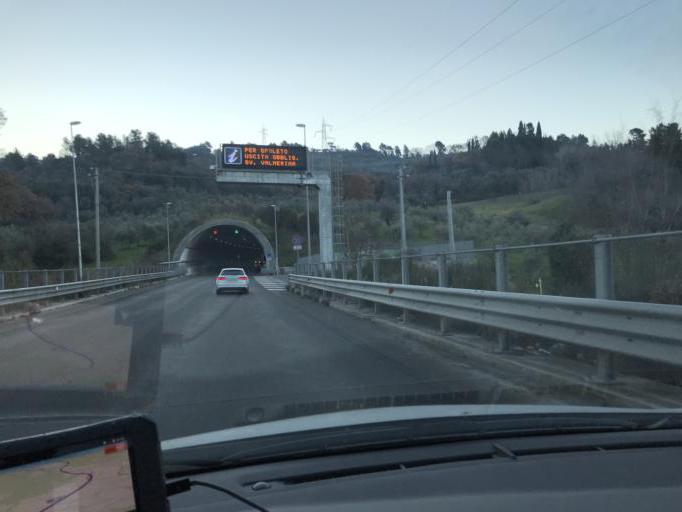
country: IT
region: Umbria
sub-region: Provincia di Terni
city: Terni
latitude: 42.5747
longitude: 12.6845
